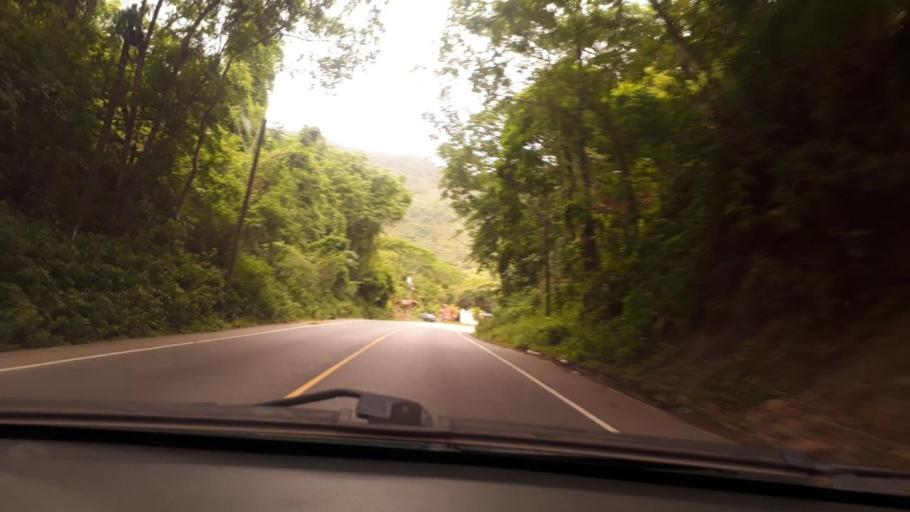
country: GT
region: Zacapa
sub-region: Municipio de Zacapa
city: Gualan
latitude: 15.1962
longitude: -89.2754
